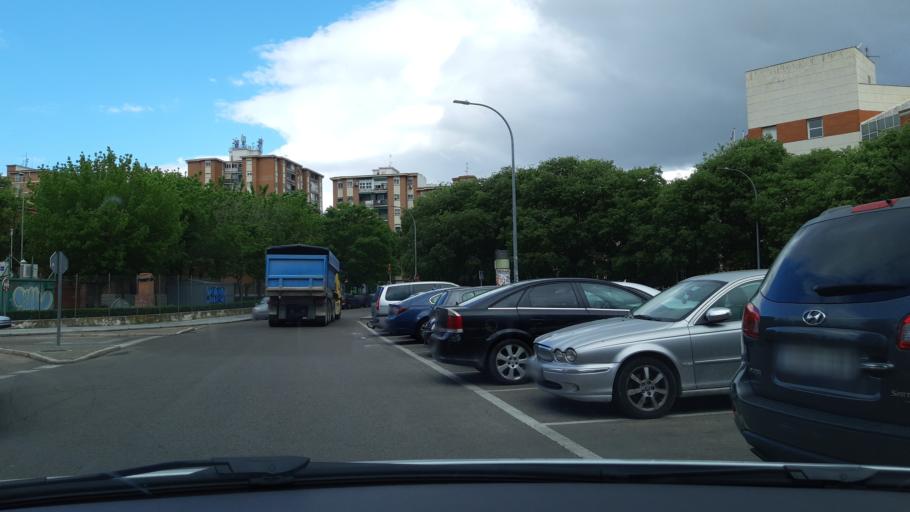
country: ES
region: Castille-La Mancha
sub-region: Provincia de Guadalajara
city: Guadalajara
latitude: 40.6302
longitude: -3.1713
